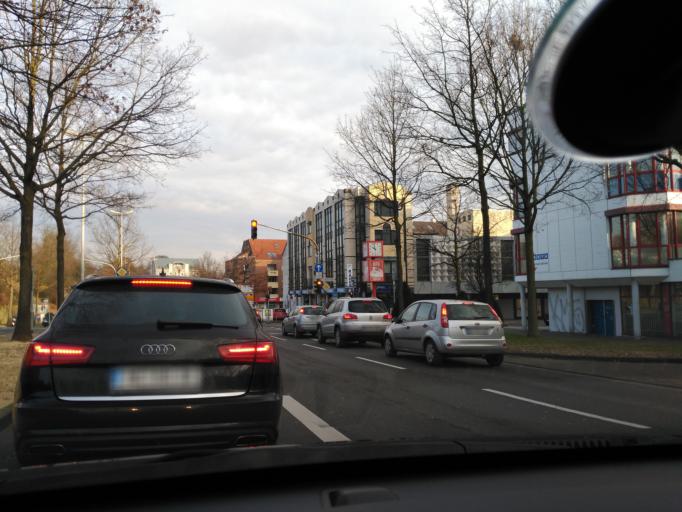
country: DE
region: North Rhine-Westphalia
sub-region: Regierungsbezirk Dusseldorf
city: Monchengladbach
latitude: 51.1653
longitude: 6.4398
